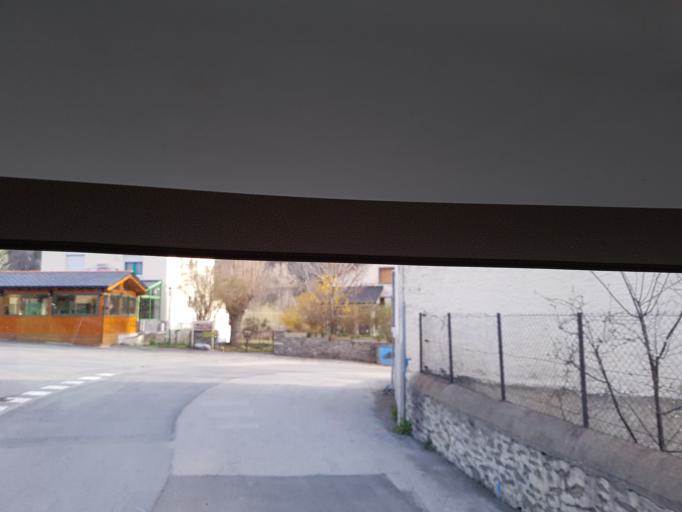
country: FR
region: Languedoc-Roussillon
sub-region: Departement des Pyrenees-Orientales
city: Osseja
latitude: 42.4397
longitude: 2.0322
